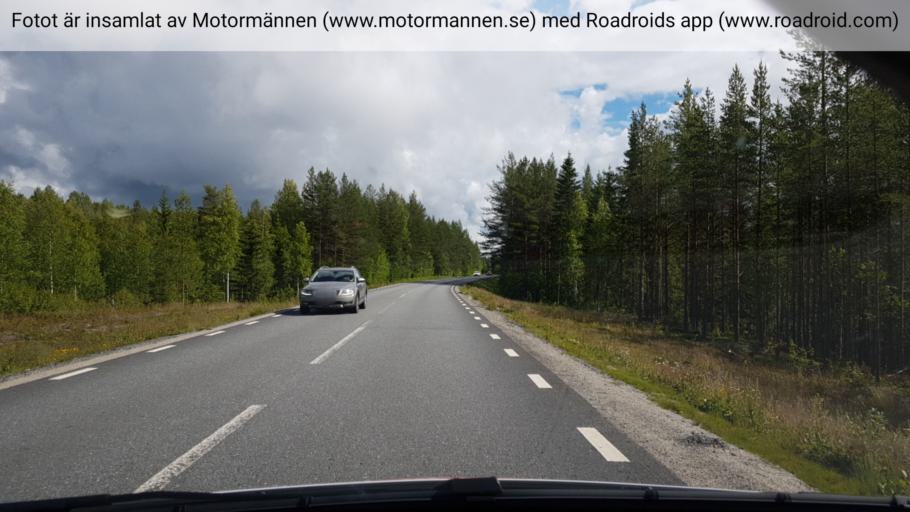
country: SE
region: Vaesterbotten
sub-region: Bjurholms Kommun
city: Bjurholm
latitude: 64.2911
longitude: 19.1894
